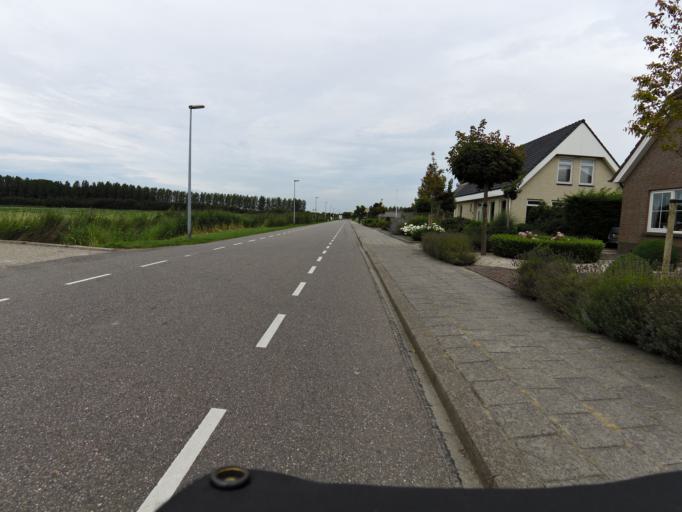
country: NL
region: South Holland
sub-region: Gemeente Goeree-Overflakkee
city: Middelharnis
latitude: 51.6949
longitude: 4.2058
